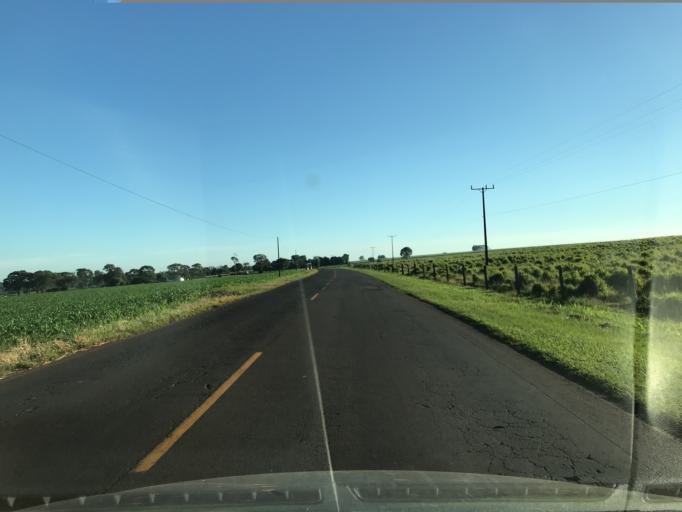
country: BR
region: Parana
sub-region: Ipora
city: Ipora
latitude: -24.1018
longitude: -53.8388
